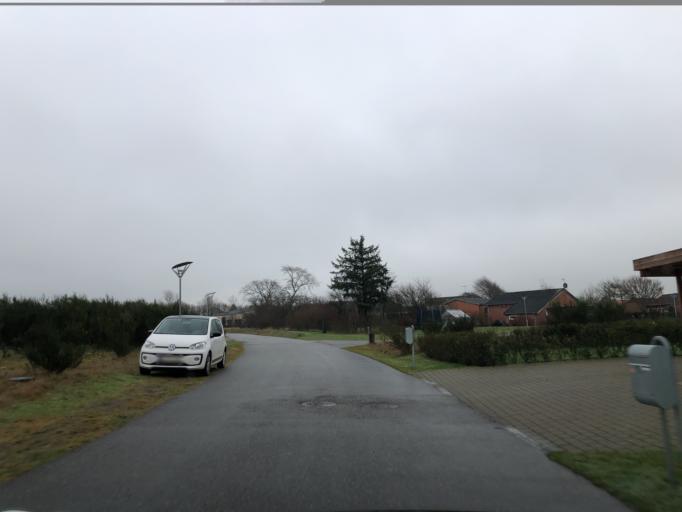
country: DK
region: Central Jutland
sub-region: Holstebro Kommune
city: Ulfborg
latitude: 56.1992
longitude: 8.3043
